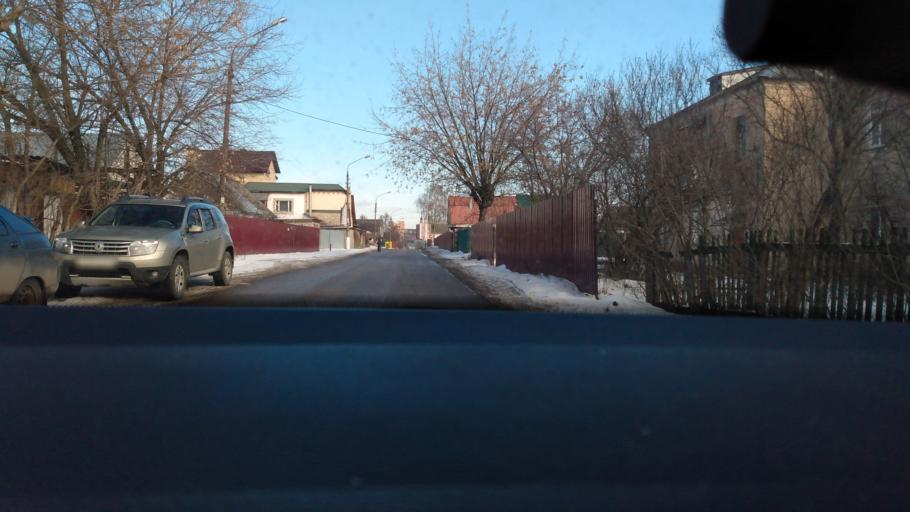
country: RU
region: Moskovskaya
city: Ramenskoye
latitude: 55.5650
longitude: 38.2103
